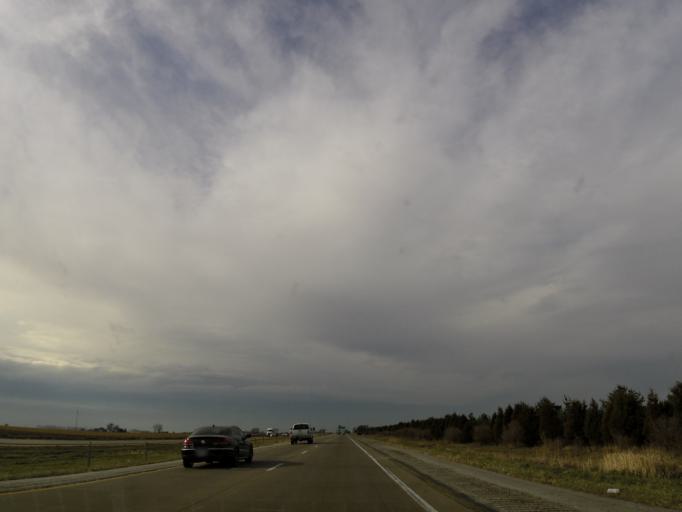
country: US
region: Iowa
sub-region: Scott County
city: Eldridge
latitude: 41.6025
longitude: -90.6542
